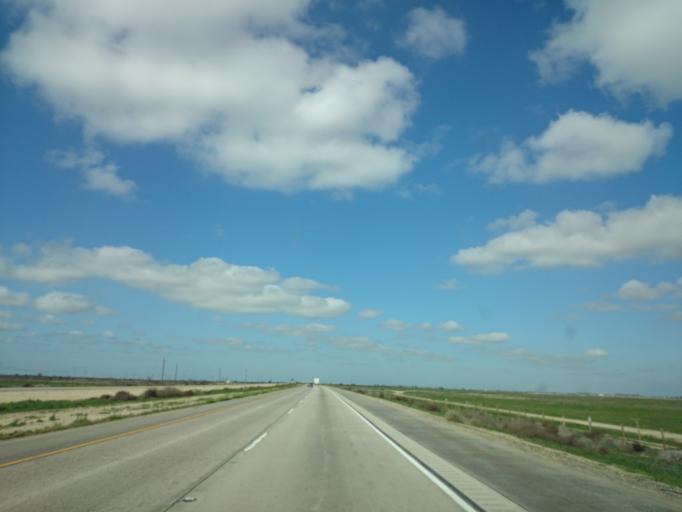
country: US
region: California
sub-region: Kern County
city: Rosedale
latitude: 35.3128
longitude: -119.2764
